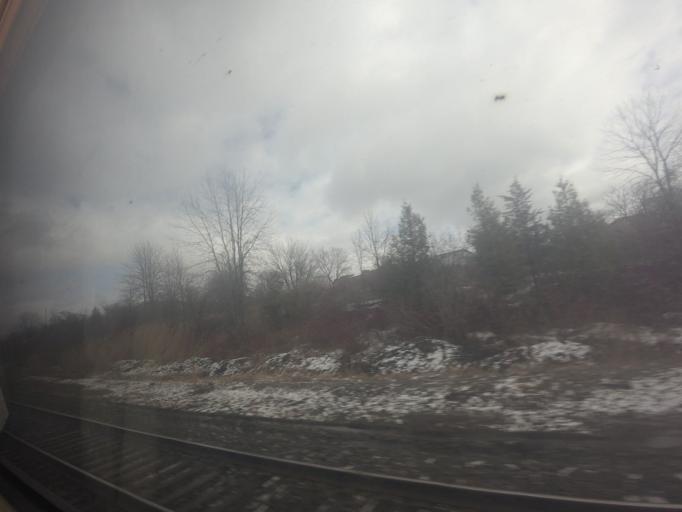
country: CA
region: Ontario
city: Ajax
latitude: 43.8089
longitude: -79.1148
